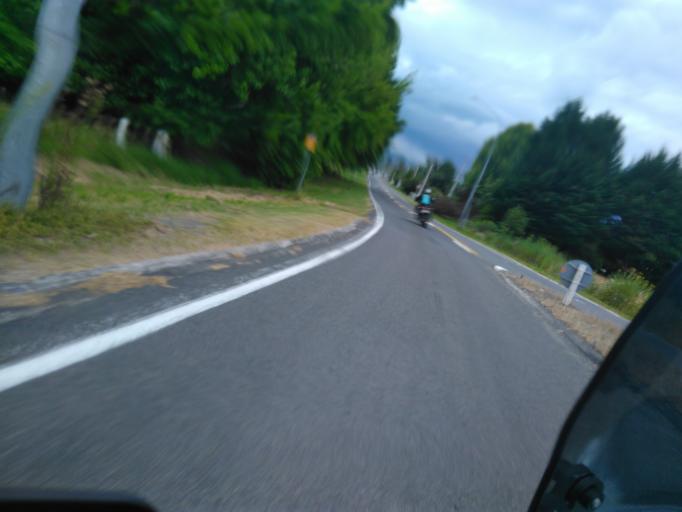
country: NZ
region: Gisborne
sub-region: Gisborne District
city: Gisborne
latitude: -38.4745
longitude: 177.8623
